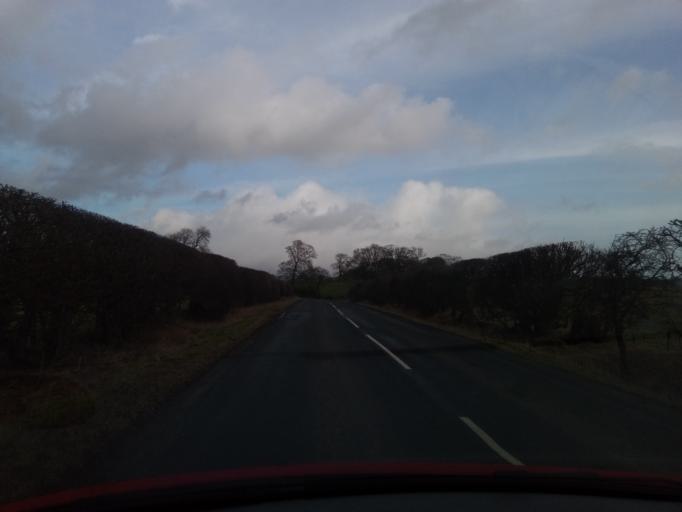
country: GB
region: England
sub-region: Northumberland
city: Rothley
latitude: 55.1261
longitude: -1.9963
